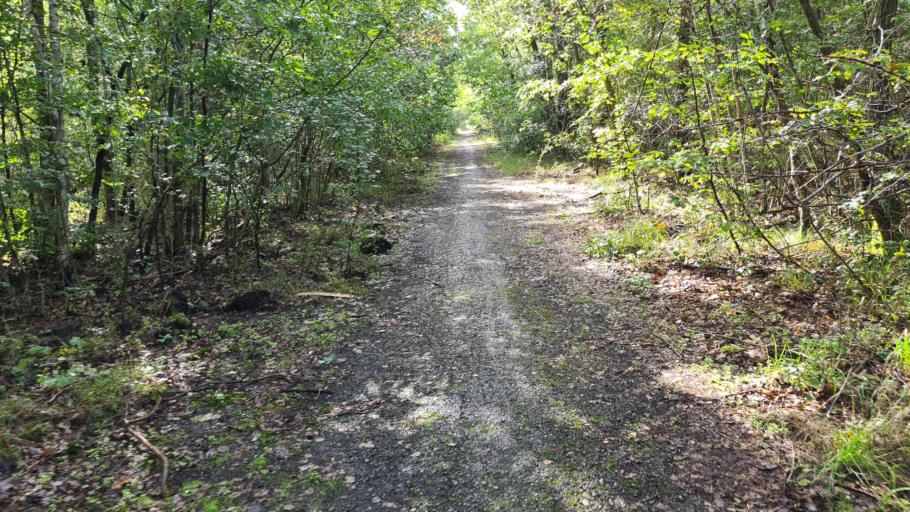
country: DE
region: Brandenburg
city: Sallgast
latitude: 51.5637
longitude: 13.8581
